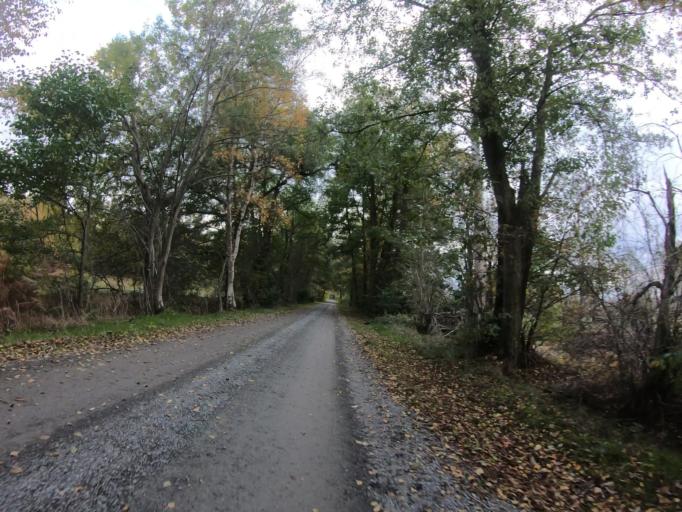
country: DE
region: Lower Saxony
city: Wagenhoff
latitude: 52.5555
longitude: 10.5581
